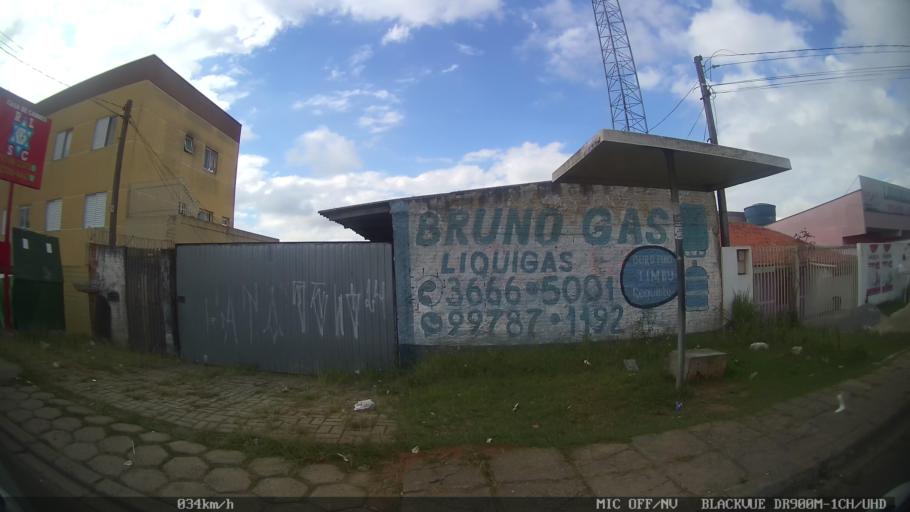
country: BR
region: Parana
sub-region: Colombo
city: Colombo
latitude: -25.3510
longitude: -49.1936
